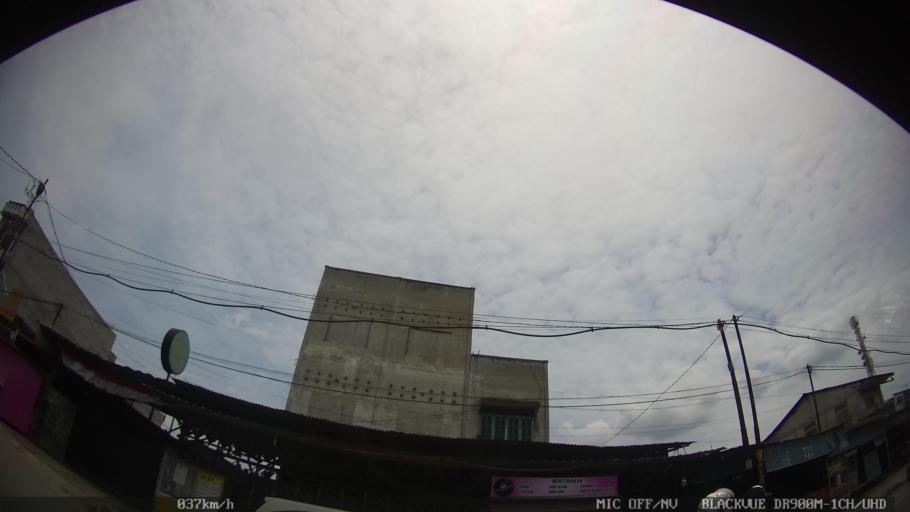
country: ID
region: North Sumatra
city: Sunggal
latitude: 3.5280
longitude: 98.6350
